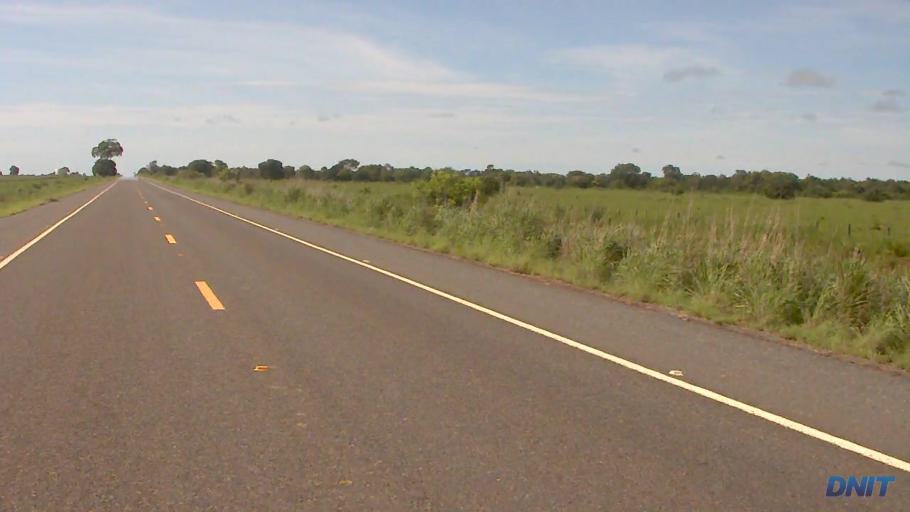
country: BR
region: Goias
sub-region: Sao Miguel Do Araguaia
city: Sao Miguel do Araguaia
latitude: -13.4216
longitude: -50.1290
